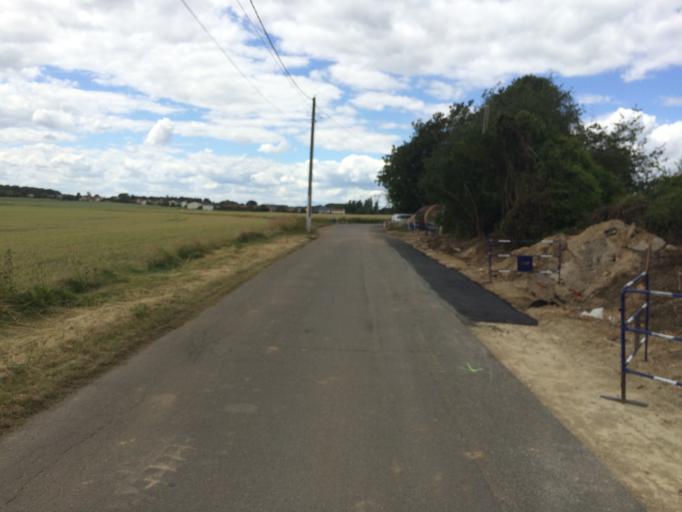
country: FR
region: Ile-de-France
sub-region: Departement de l'Essonne
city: Les Ulis
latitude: 48.6721
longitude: 2.1823
